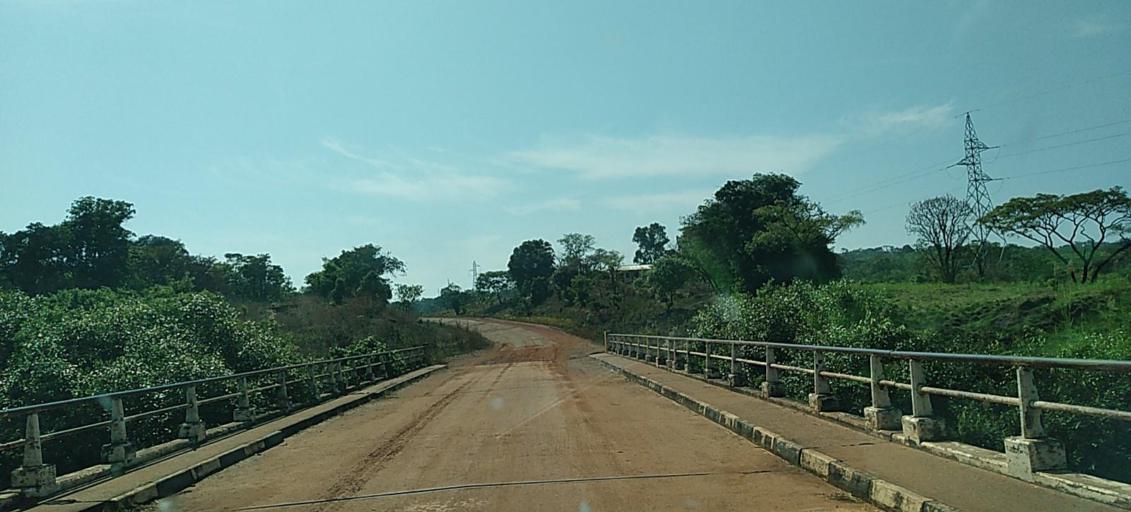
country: ZM
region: North-Western
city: Mwinilunga
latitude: -11.8254
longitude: 25.1256
